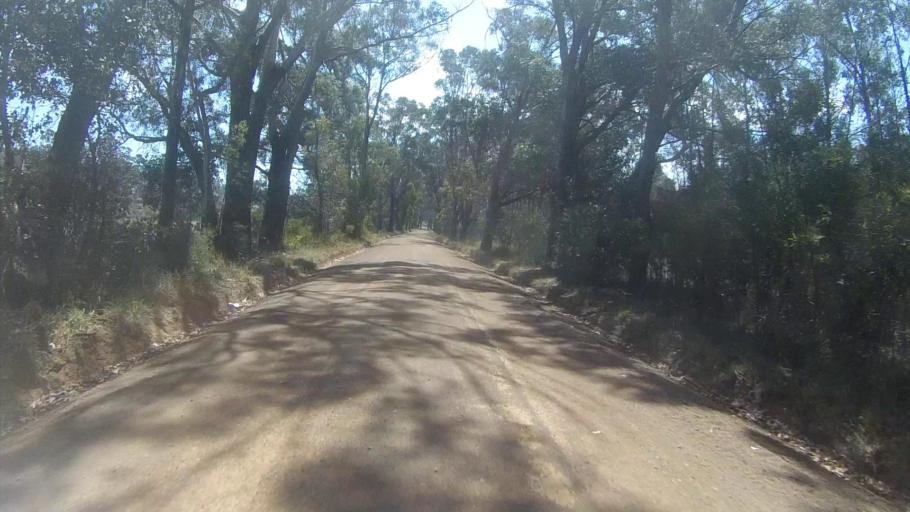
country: AU
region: Tasmania
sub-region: Sorell
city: Sorell
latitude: -42.8547
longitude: 147.8325
